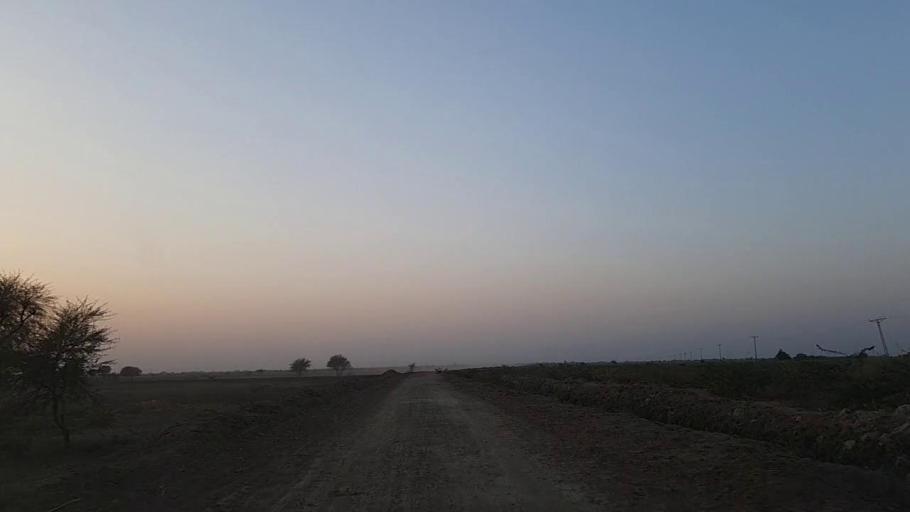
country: PK
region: Sindh
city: Naukot
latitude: 24.8917
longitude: 69.3623
